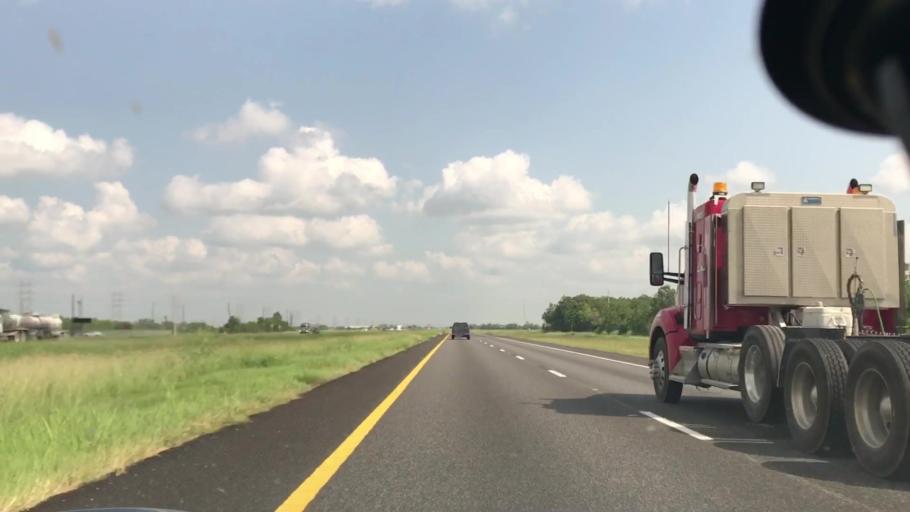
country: US
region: Texas
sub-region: Brazoria County
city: Rosharon
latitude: 29.4025
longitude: -95.4268
